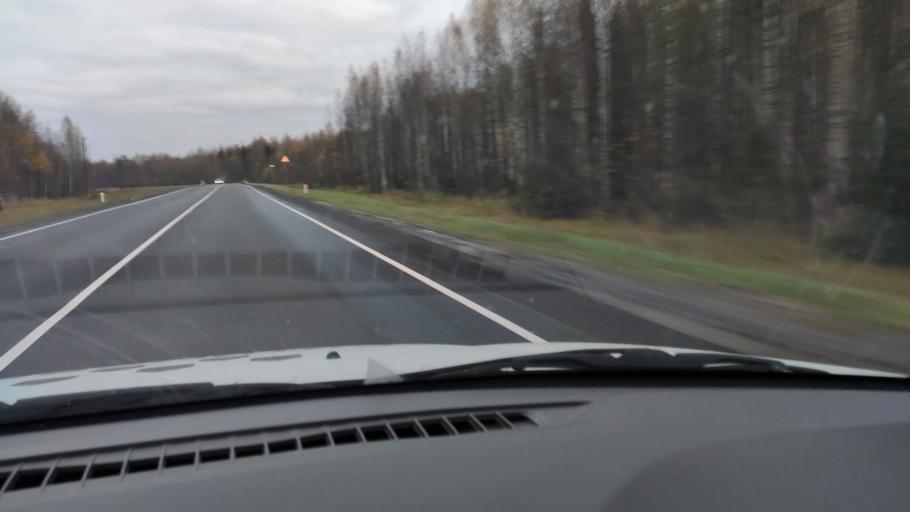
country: RU
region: Kirov
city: Lesnyye Polyany
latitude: 58.8018
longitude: 52.5770
